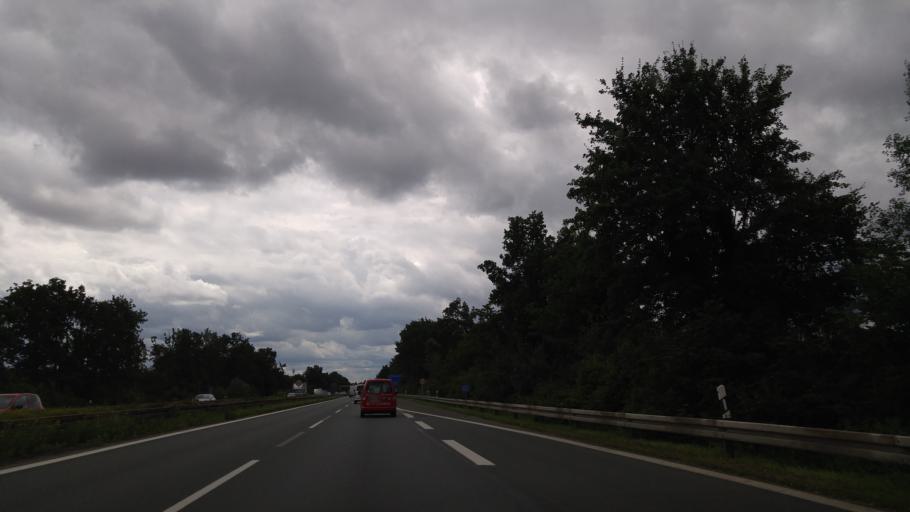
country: DE
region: Bavaria
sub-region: Regierungsbezirk Mittelfranken
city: Furth
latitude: 49.4918
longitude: 11.0009
